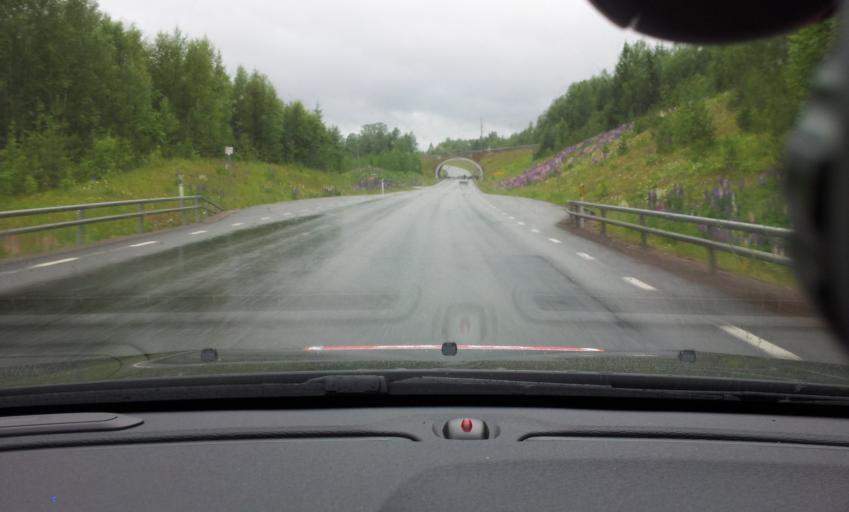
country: SE
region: Jaemtland
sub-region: Ragunda Kommun
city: Hammarstrand
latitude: 63.0326
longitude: 16.5905
